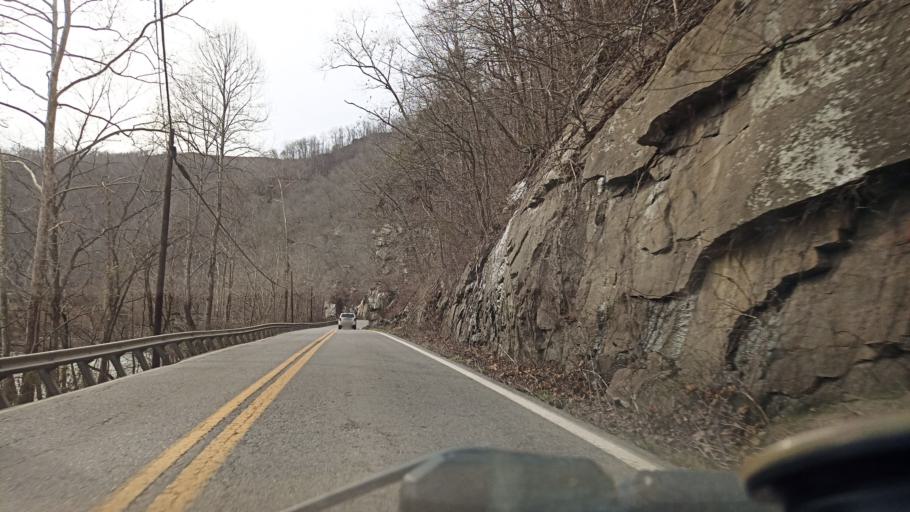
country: US
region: West Virginia
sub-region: Mingo County
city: Gilbert Creek
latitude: 37.6418
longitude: -81.8733
